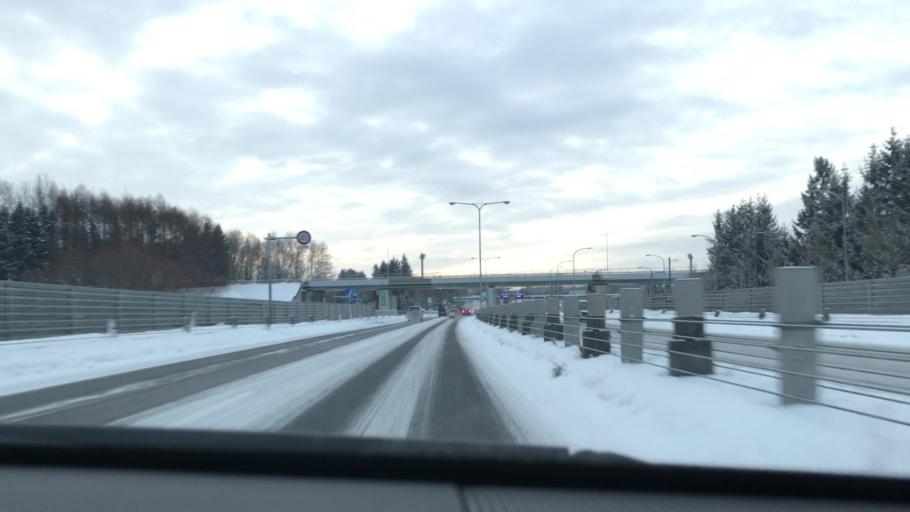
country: JP
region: Hokkaido
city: Kitahiroshima
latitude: 43.0182
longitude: 141.4621
